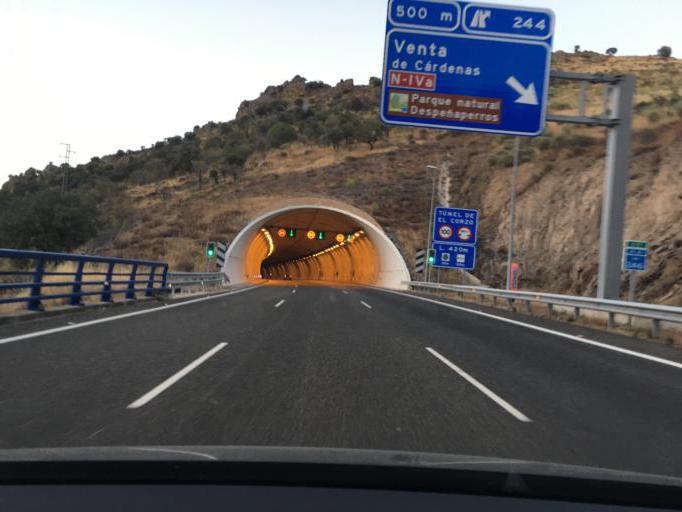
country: ES
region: Andalusia
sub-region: Provincia de Jaen
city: Santa Elena
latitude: 38.4017
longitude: -3.4982
